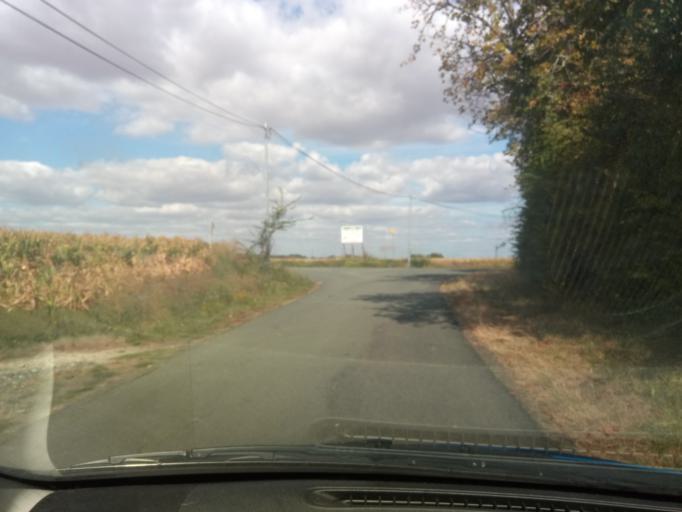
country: FR
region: Poitou-Charentes
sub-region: Departement de la Vienne
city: Montmorillon
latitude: 46.4932
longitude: 0.8129
